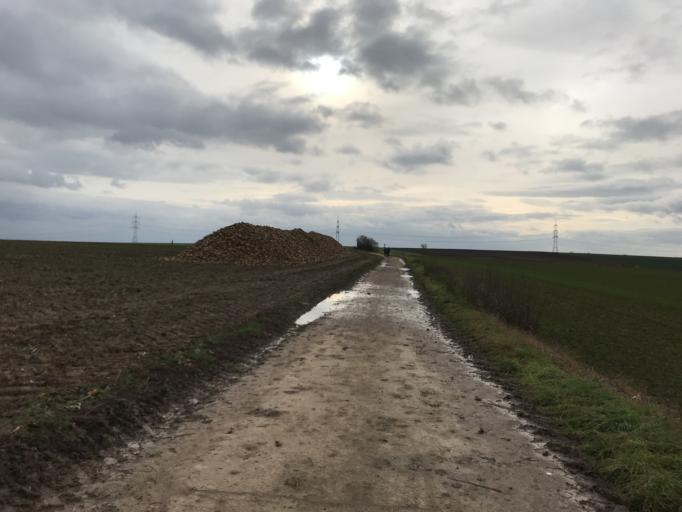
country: DE
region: Rheinland-Pfalz
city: Mainz
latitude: 49.9581
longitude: 8.2921
